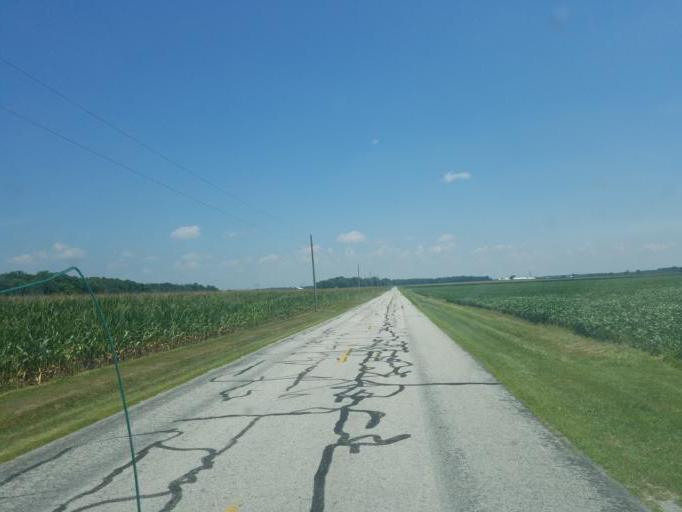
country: US
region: Ohio
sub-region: Auglaize County
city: Wapakoneta
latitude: 40.5404
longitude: -84.2568
